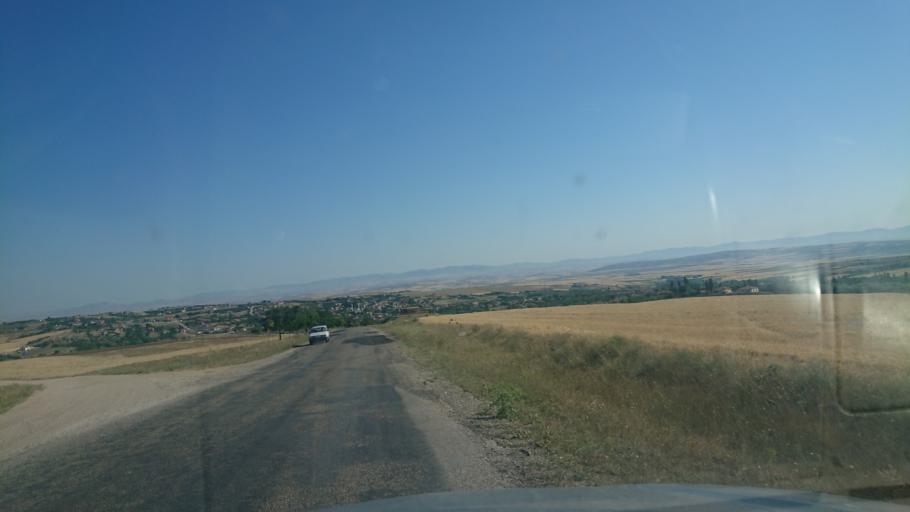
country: TR
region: Aksaray
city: Agacoren
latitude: 38.8547
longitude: 33.9515
